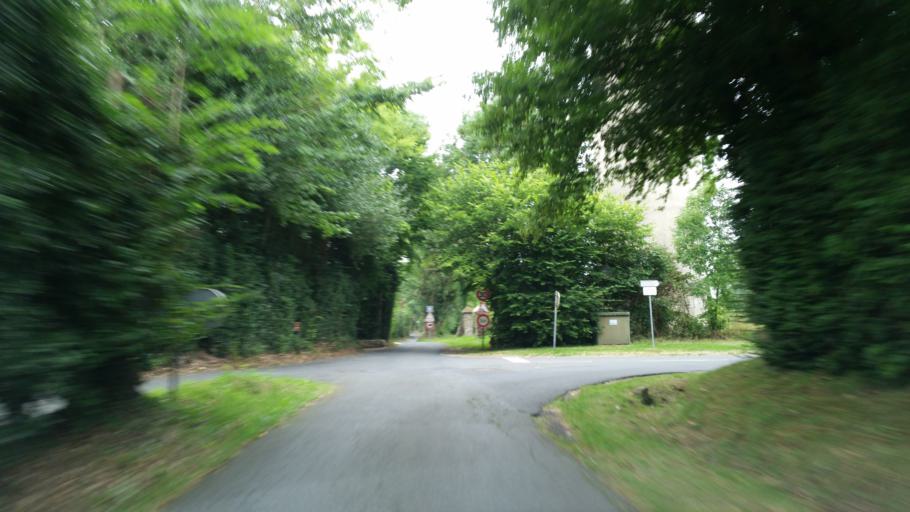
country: FR
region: Lower Normandy
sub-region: Departement du Calvados
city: Honfleur
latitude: 49.4080
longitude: 0.2335
